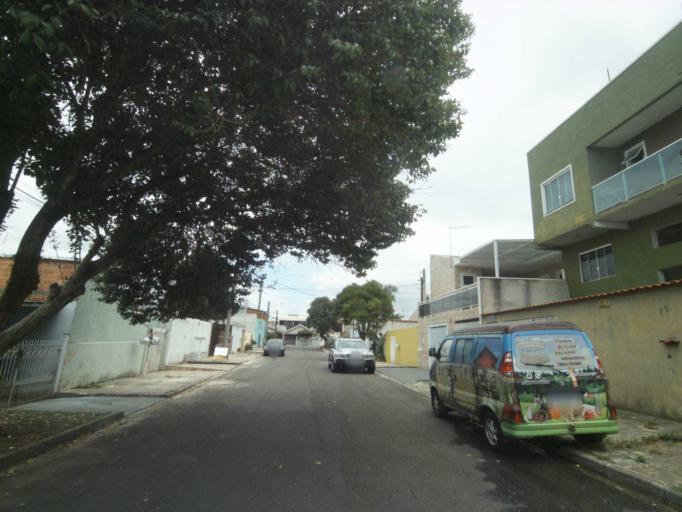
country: BR
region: Parana
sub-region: Sao Jose Dos Pinhais
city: Sao Jose dos Pinhais
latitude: -25.5433
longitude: -49.2526
